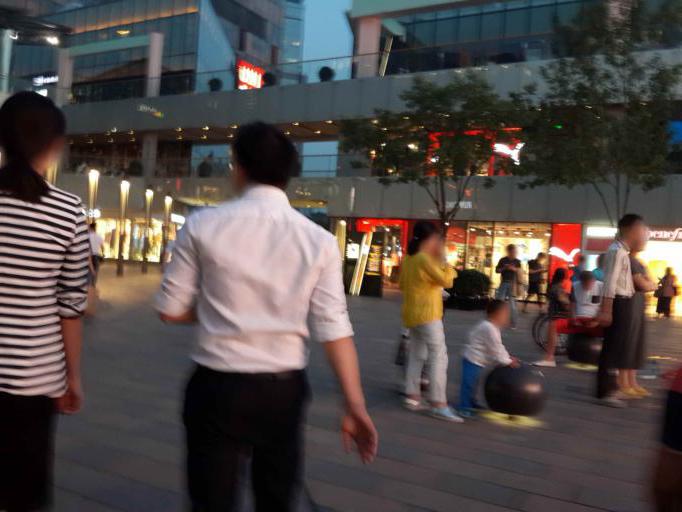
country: CN
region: Beijing
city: Chaowai
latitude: 39.9335
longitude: 116.4482
